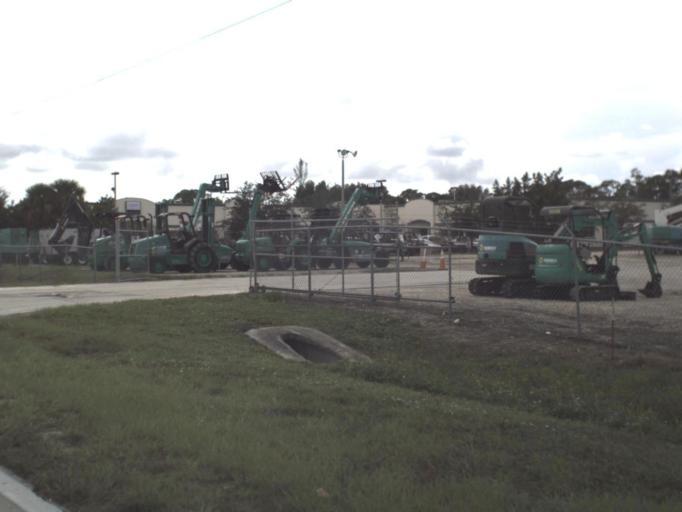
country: US
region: Florida
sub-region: Lee County
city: Villas
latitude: 26.5570
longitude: -81.8530
